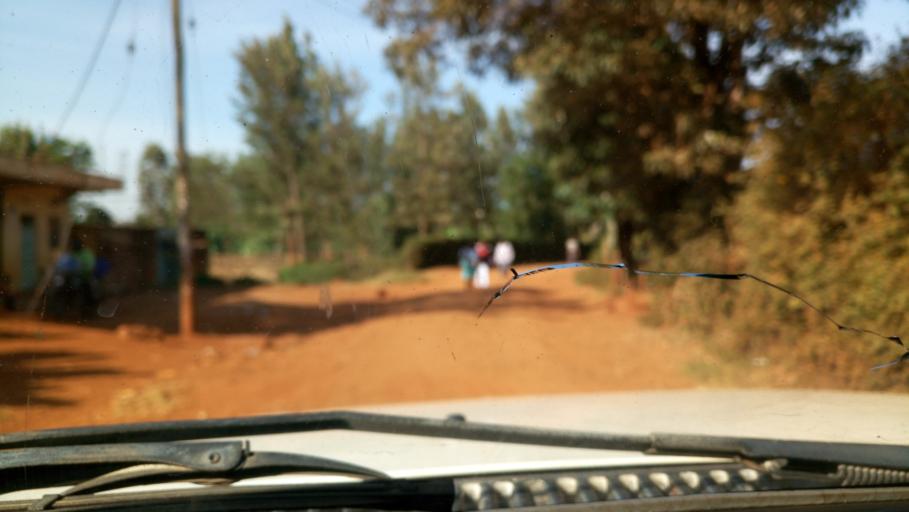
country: KE
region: Murang'a District
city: Murang'a
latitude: -0.7292
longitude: 37.1540
